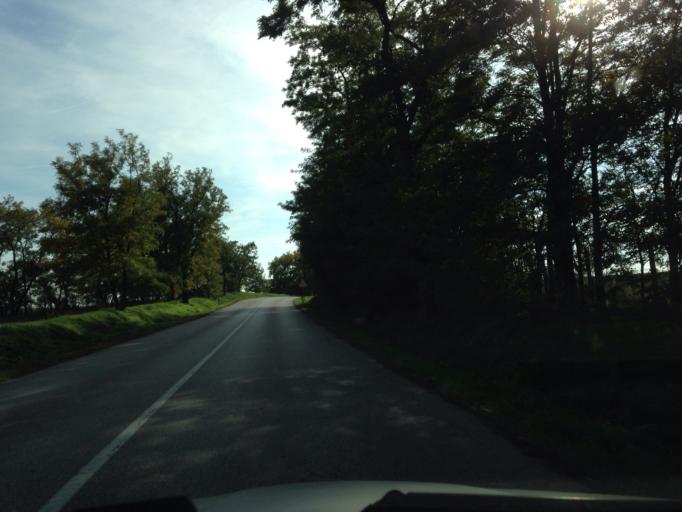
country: SK
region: Nitriansky
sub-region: Okres Komarno
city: Hurbanovo
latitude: 47.8578
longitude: 18.2742
